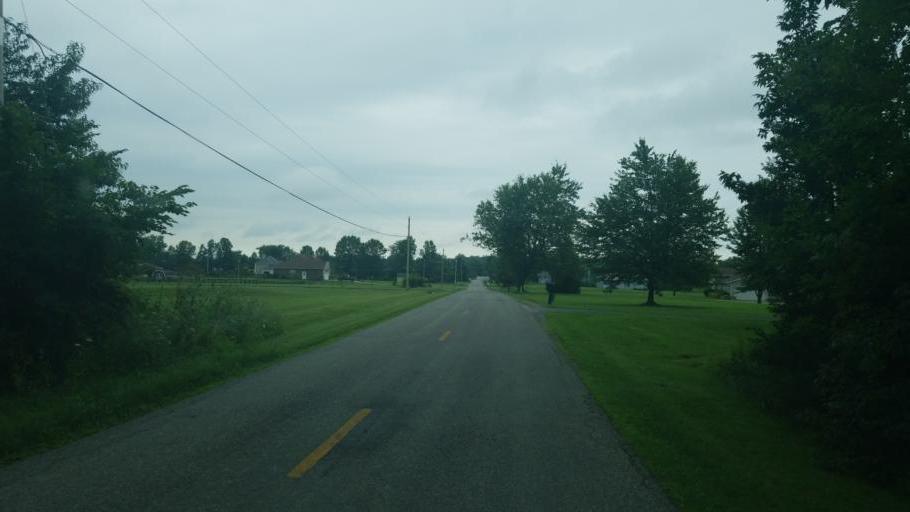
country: US
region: Ohio
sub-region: Delaware County
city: Sunbury
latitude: 40.3191
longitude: -82.8672
